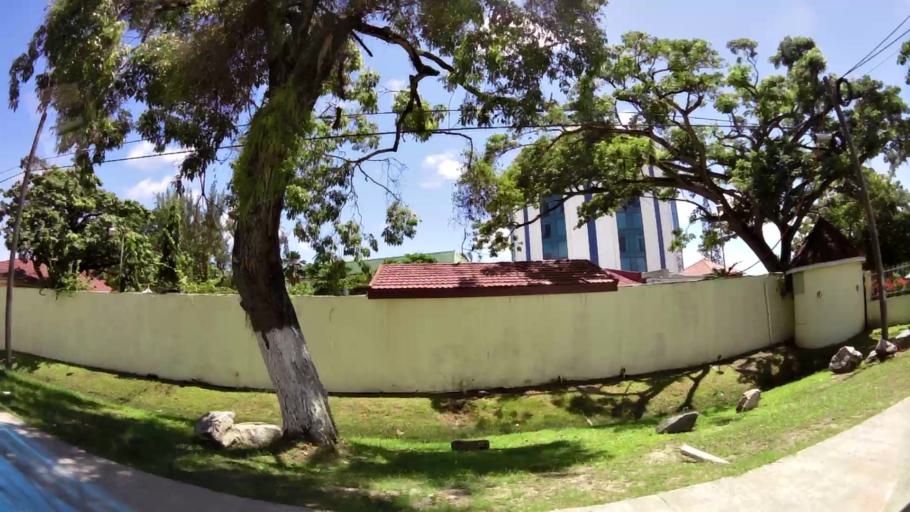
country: GY
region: Demerara-Mahaica
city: Georgetown
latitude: 6.8247
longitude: -58.1621
